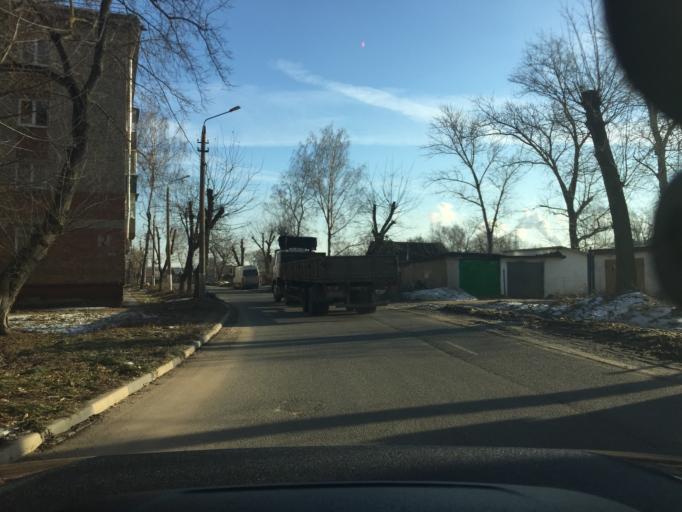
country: RU
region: Tula
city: Tula
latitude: 54.1777
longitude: 37.7061
